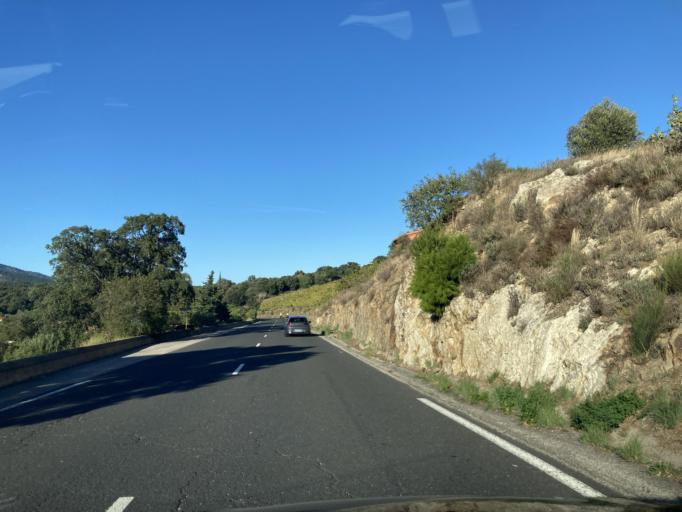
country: FR
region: Languedoc-Roussillon
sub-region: Departement des Pyrenees-Orientales
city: Collioure
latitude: 42.5255
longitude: 3.0729
